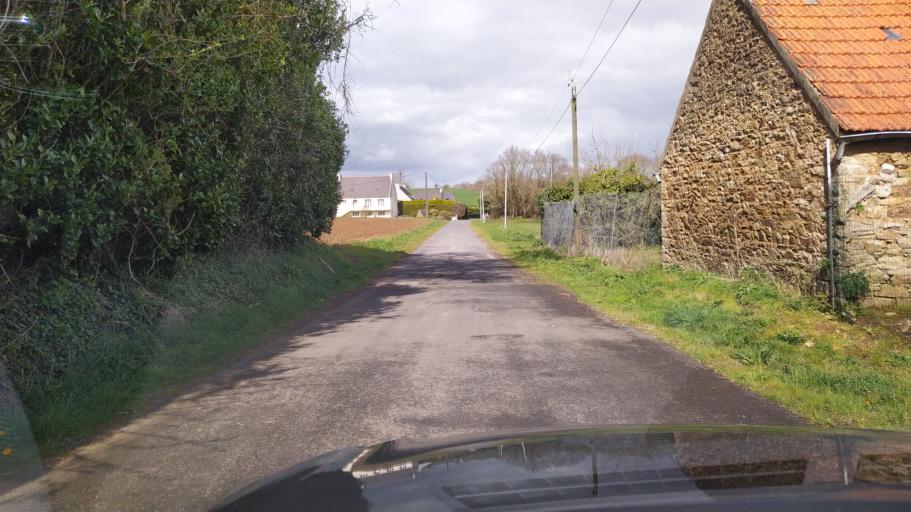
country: FR
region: Brittany
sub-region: Departement du Finistere
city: Bodilis
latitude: 48.5177
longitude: -4.1194
